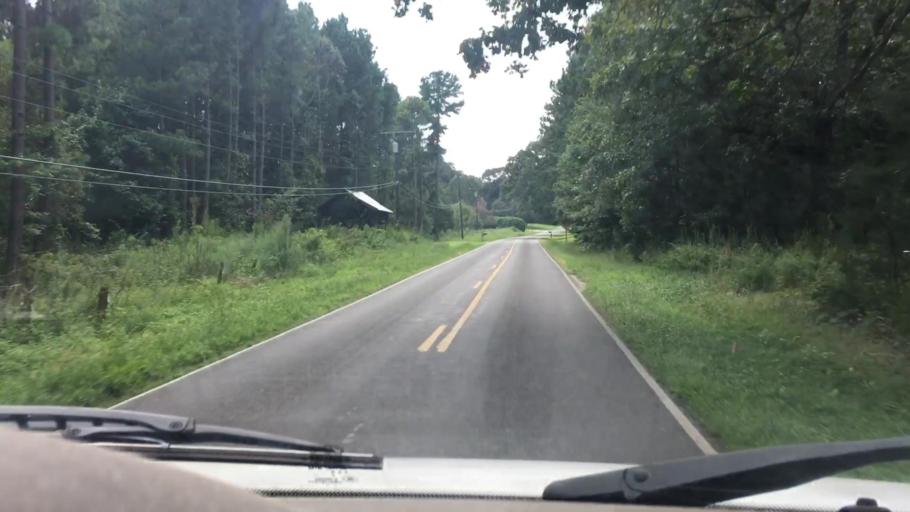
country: US
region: North Carolina
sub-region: Iredell County
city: Mooresville
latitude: 35.6609
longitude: -80.8008
